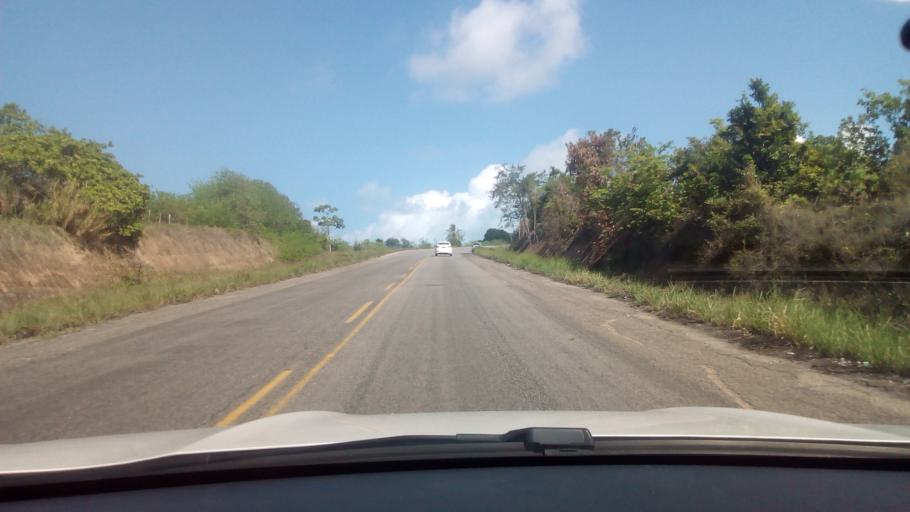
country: BR
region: Paraiba
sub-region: Conde
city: Conde
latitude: -7.2403
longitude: -34.8363
